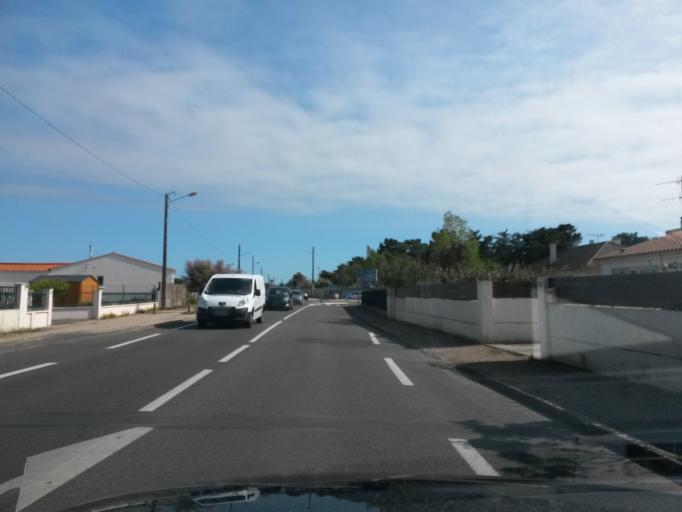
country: FR
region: Pays de la Loire
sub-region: Departement de la Vendee
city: Olonne-sur-Mer
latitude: 46.5474
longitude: -1.8049
